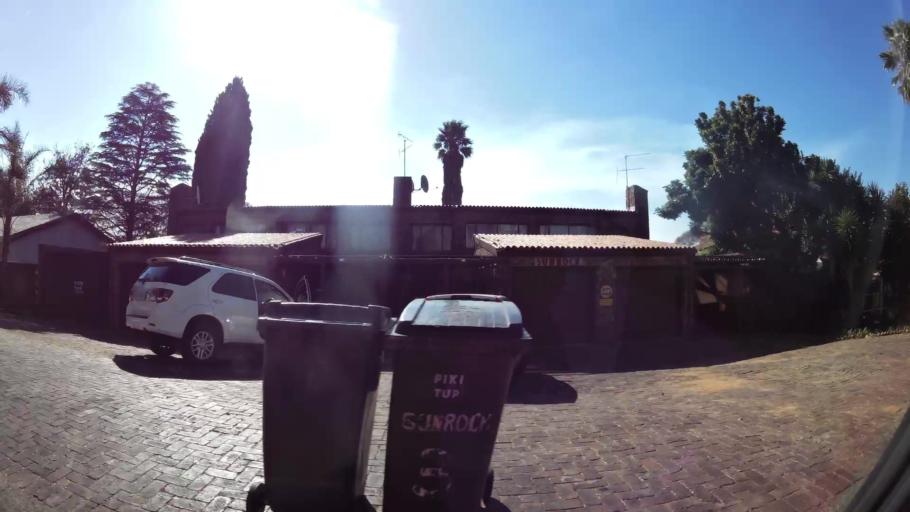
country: ZA
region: Gauteng
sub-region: City of Johannesburg Metropolitan Municipality
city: Roodepoort
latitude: -26.1204
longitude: 27.9645
